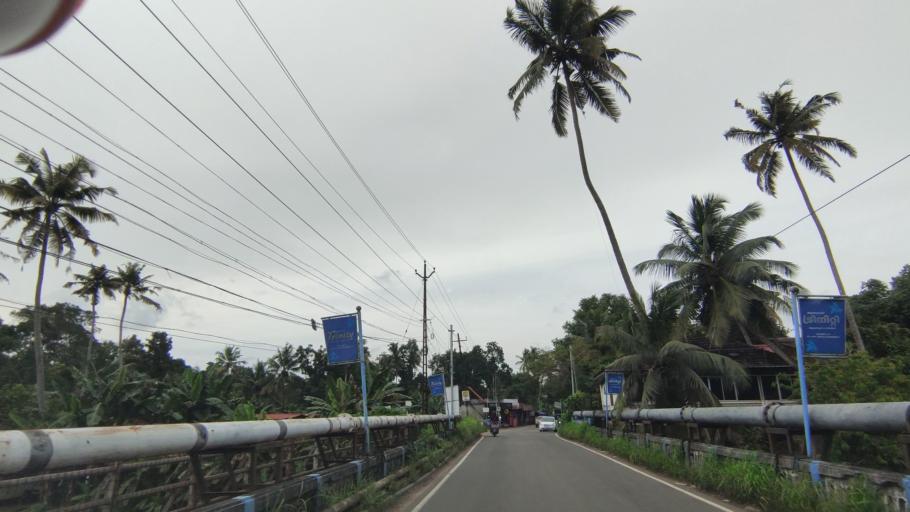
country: IN
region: Kerala
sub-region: Kottayam
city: Kottayam
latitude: 9.6256
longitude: 76.5123
